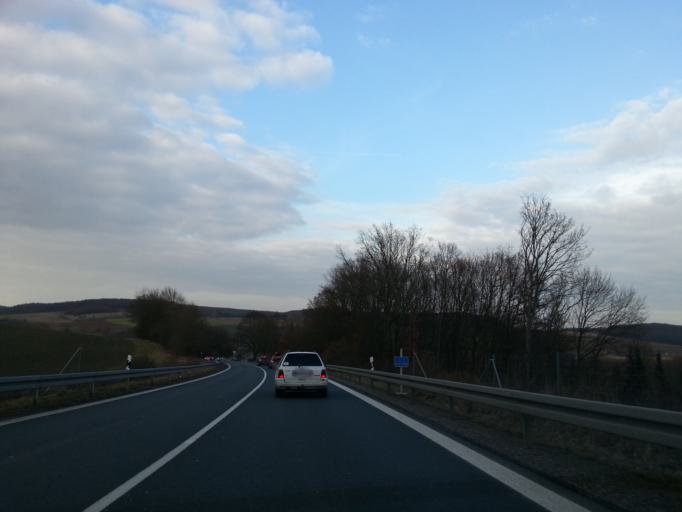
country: DE
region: Bavaria
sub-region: Regierungsbezirk Unterfranken
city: Waldbrunn
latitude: 49.7698
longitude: 9.7740
